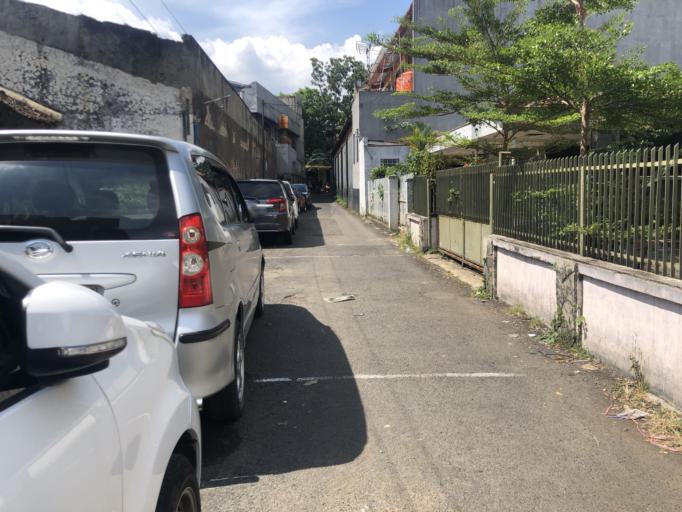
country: ID
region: West Java
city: Bandung
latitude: -6.9324
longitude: 107.6127
